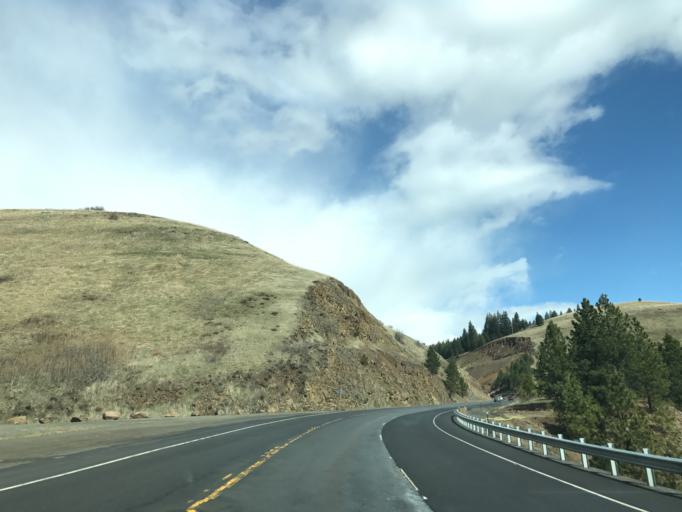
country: US
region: Idaho
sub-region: Idaho County
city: Grangeville
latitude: 45.8374
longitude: -116.2393
